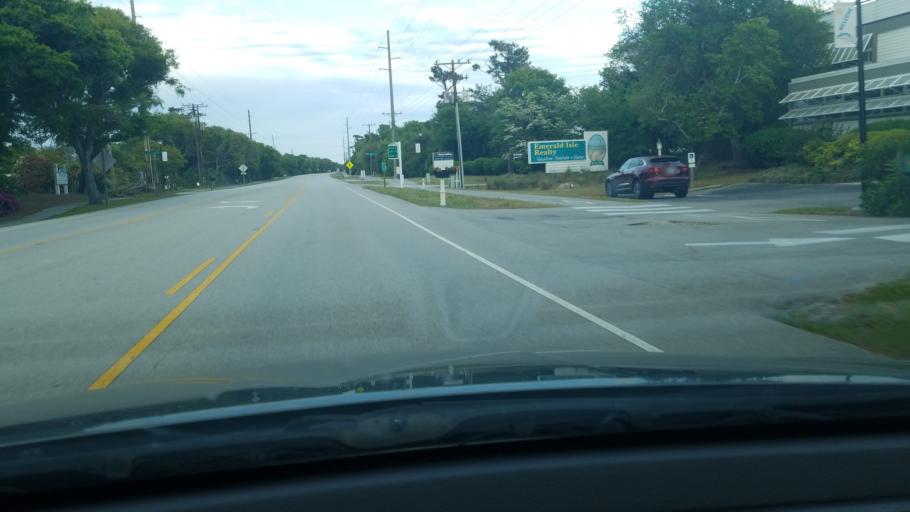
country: US
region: North Carolina
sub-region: Carteret County
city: Cape Carteret
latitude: 34.6664
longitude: -77.0273
